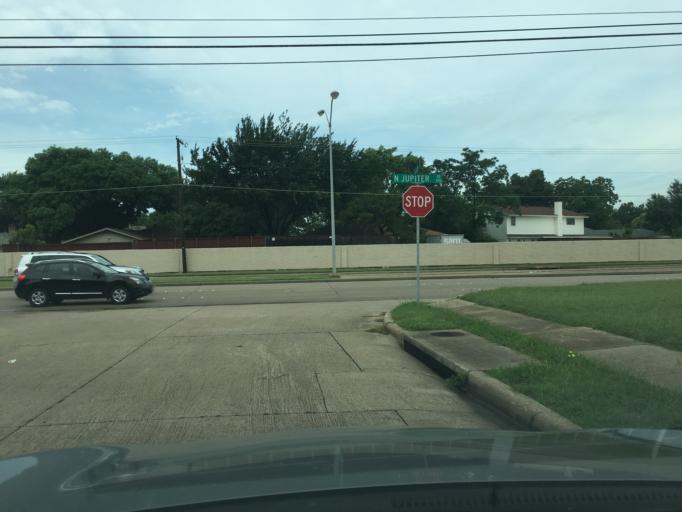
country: US
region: Texas
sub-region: Dallas County
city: Richardson
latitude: 32.9509
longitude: -96.6824
